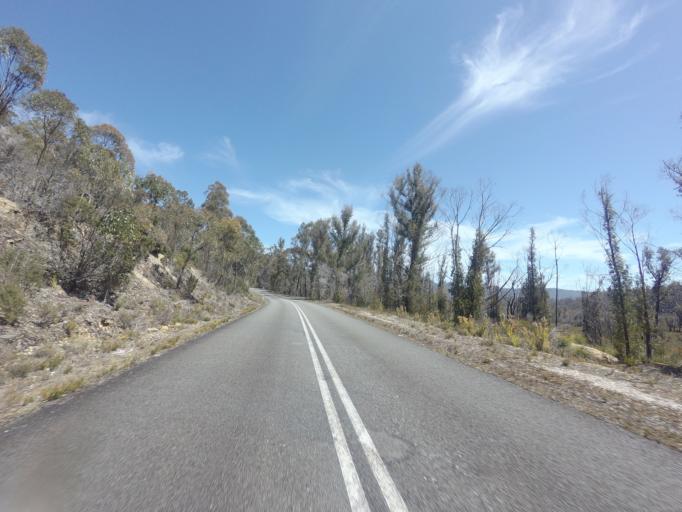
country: AU
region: Tasmania
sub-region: Huon Valley
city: Geeveston
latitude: -42.8448
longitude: 146.2481
